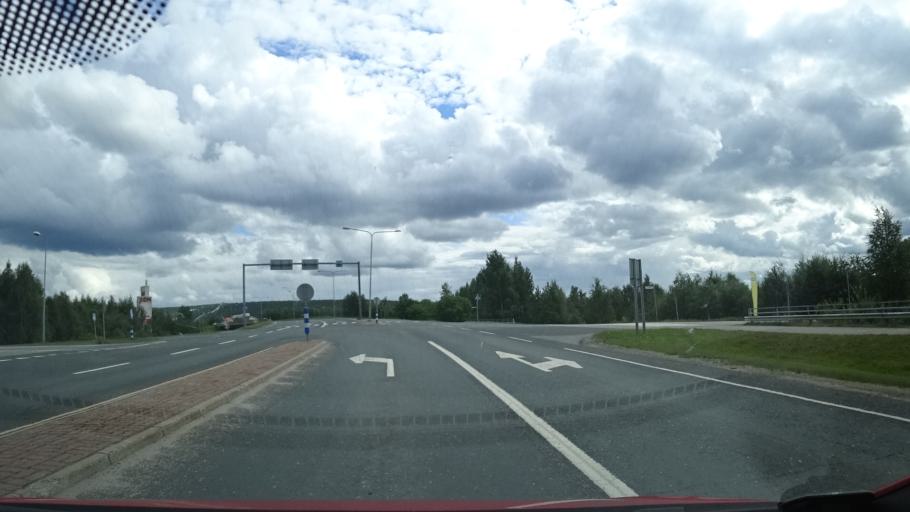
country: FI
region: Lapland
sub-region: Rovaniemi
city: Rovaniemi
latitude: 66.5199
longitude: 25.7476
